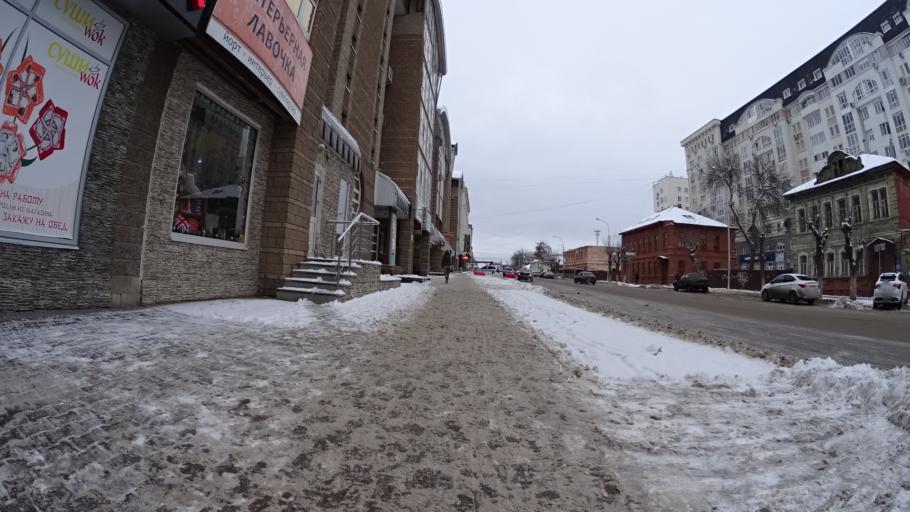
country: RU
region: Bashkortostan
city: Ufa
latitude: 54.7290
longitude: 55.9453
